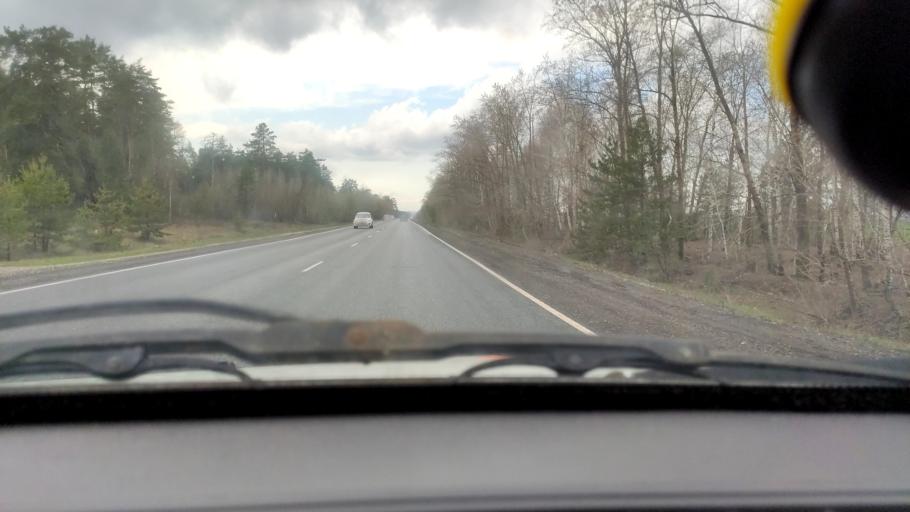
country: RU
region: Samara
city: Povolzhskiy
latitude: 53.6231
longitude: 49.6457
